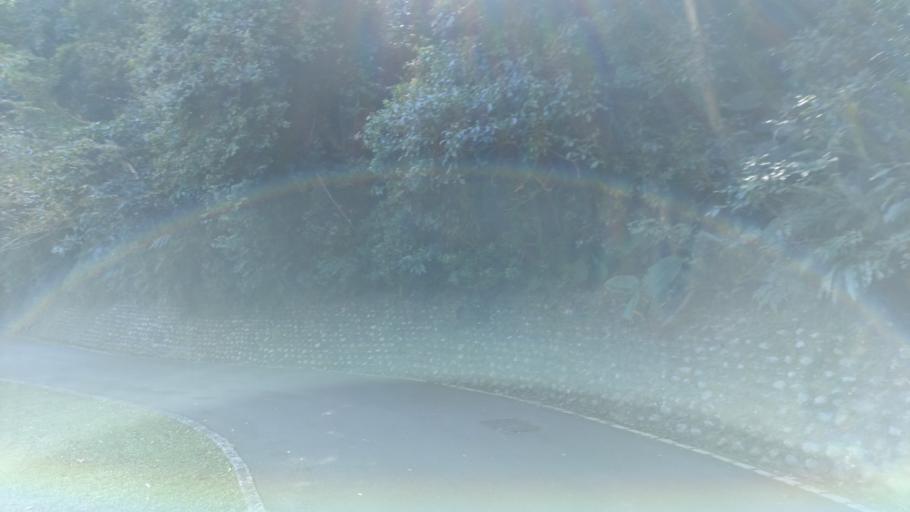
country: TW
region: Taiwan
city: Daxi
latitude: 24.8439
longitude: 121.3019
